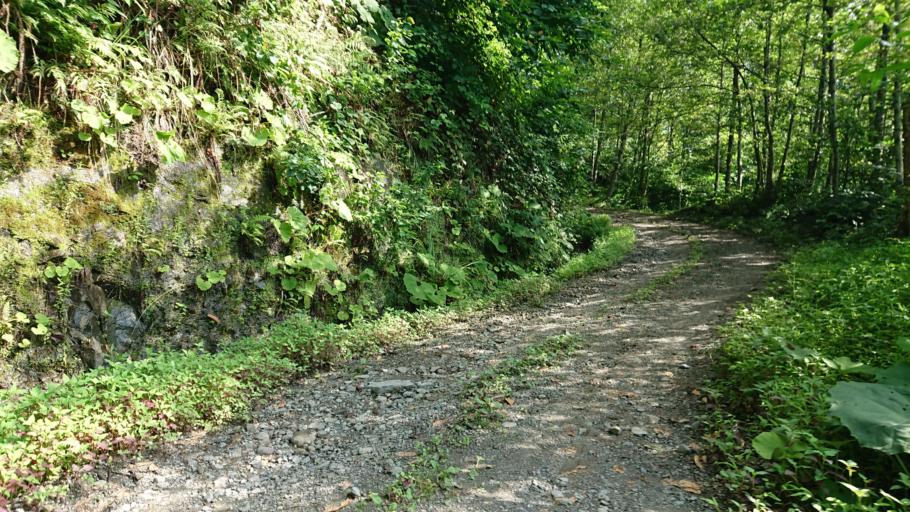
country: TR
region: Rize
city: Rize
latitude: 40.9771
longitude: 40.4989
